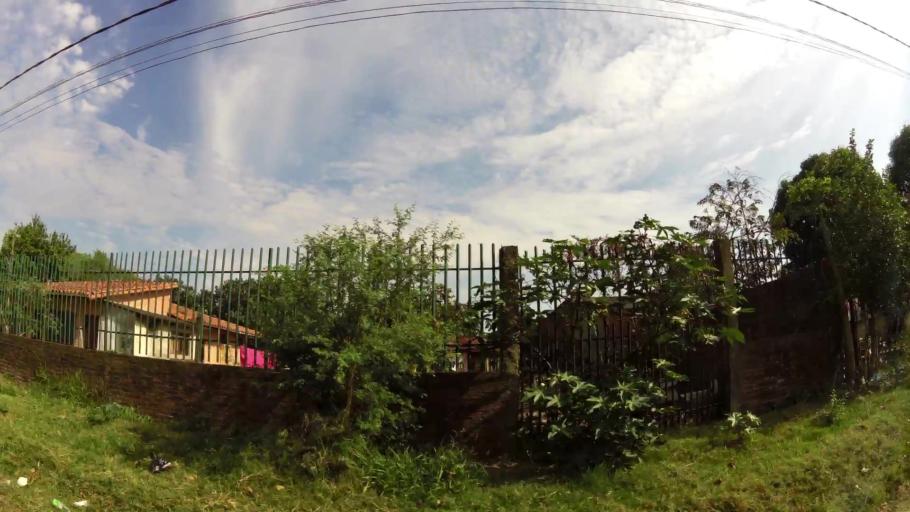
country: BO
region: Santa Cruz
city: Santa Cruz de la Sierra
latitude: -17.7360
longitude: -63.1353
